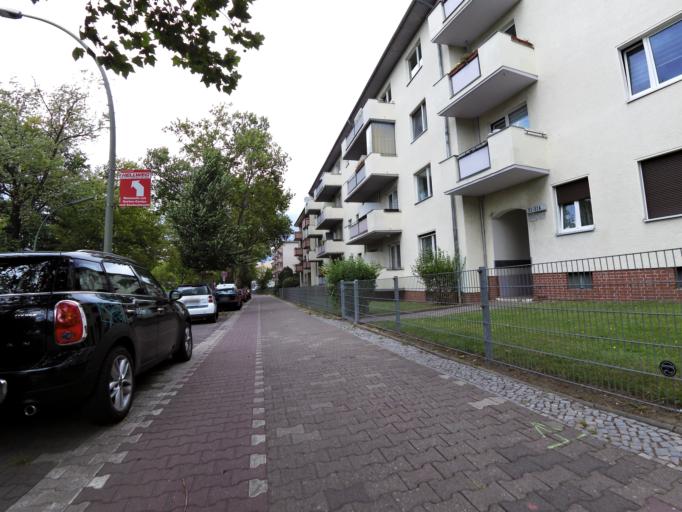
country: DE
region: Berlin
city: Mariendorf
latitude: 52.4396
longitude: 13.3818
